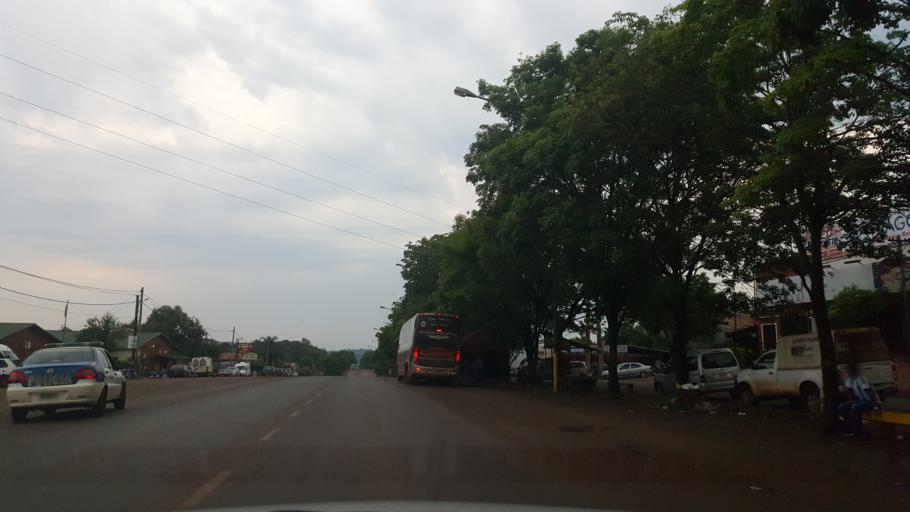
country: AR
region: Misiones
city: Jardin America
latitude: -27.0393
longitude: -55.2301
